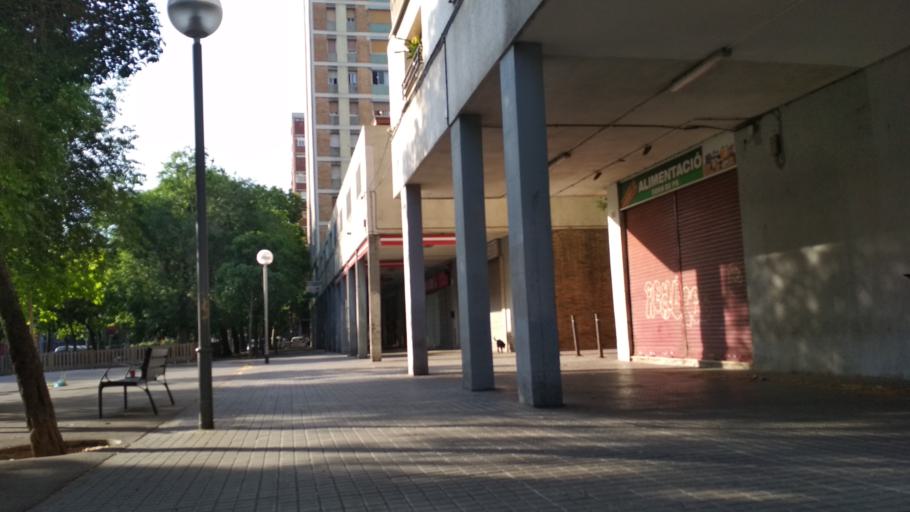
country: ES
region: Catalonia
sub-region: Provincia de Barcelona
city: Sant Marti
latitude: 41.4173
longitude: 2.2130
